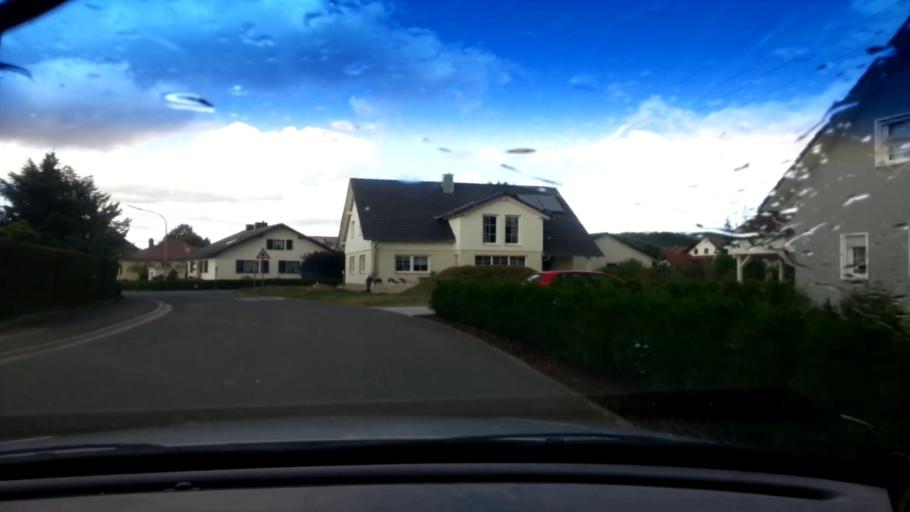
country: DE
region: Bavaria
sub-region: Upper Franconia
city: Zapfendorf
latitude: 50.0201
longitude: 10.9387
